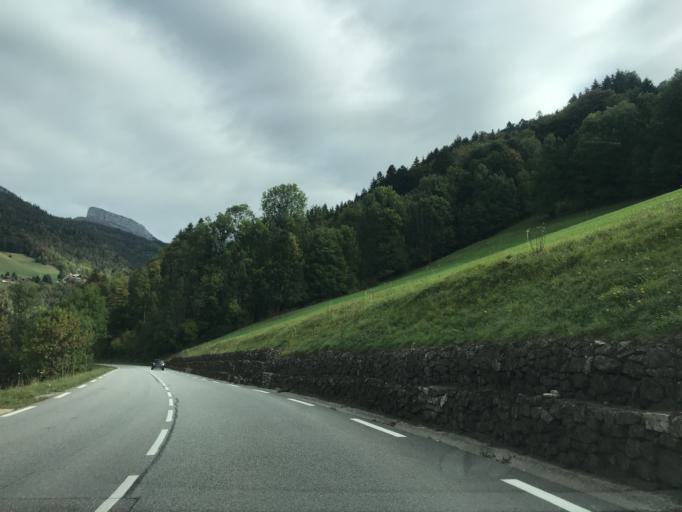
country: FR
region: Rhone-Alpes
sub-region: Departement de la Haute-Savoie
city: Saint-Jean-de-Sixt
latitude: 45.9262
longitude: 6.4116
